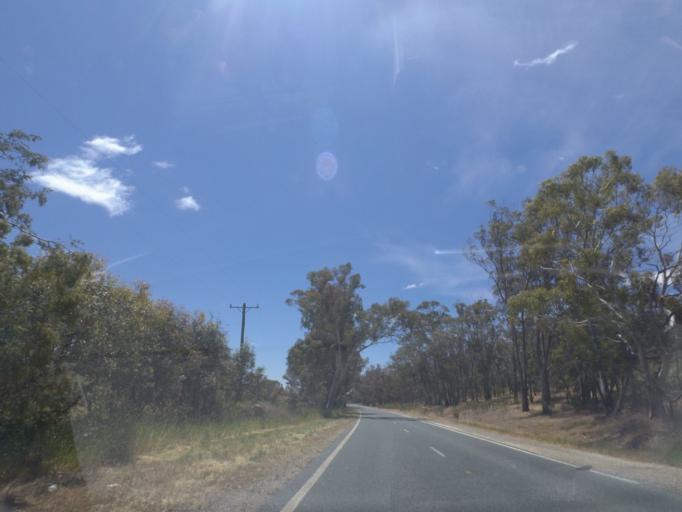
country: AU
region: Victoria
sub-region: Mount Alexander
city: Castlemaine
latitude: -37.1852
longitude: 144.1483
